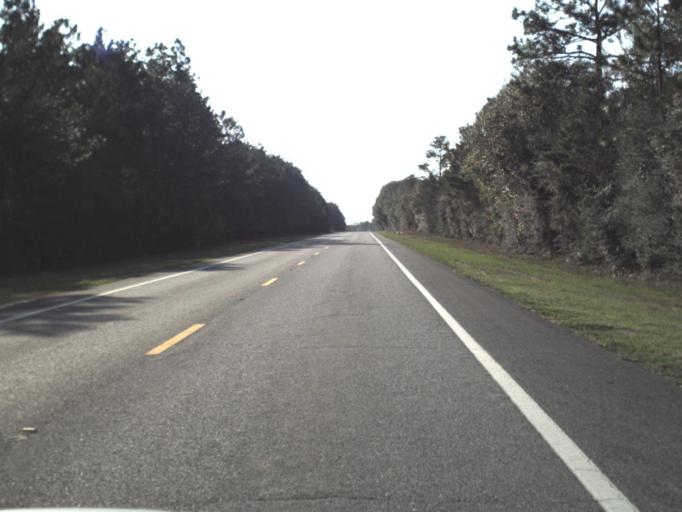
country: US
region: Florida
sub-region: Bay County
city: Youngstown
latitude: 30.4366
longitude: -85.5086
